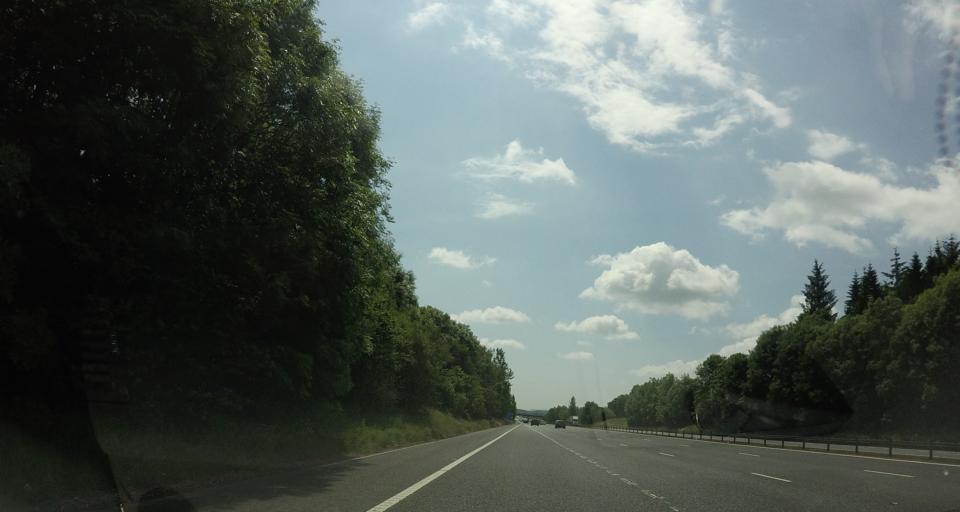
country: GB
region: Scotland
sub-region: Dumfries and Galloway
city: Lochmaben
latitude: 55.2154
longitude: -3.4126
